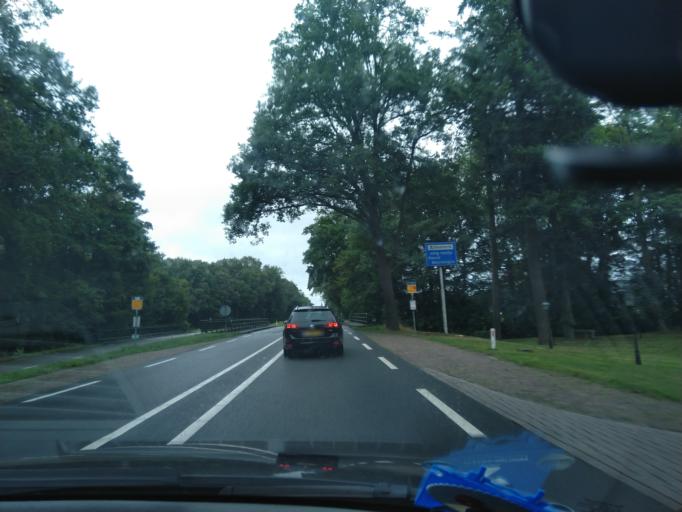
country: NL
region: Overijssel
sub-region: Gemeente Oldenzaal
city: Oldenzaal
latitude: 52.3655
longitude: 6.9940
